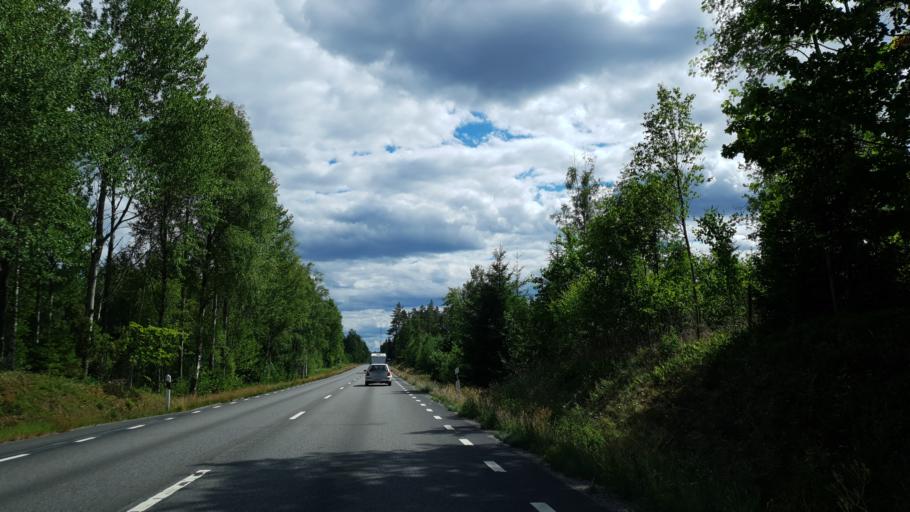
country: SE
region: Kronoberg
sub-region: Lessebo Kommun
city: Lessebo
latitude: 56.7922
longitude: 15.4131
